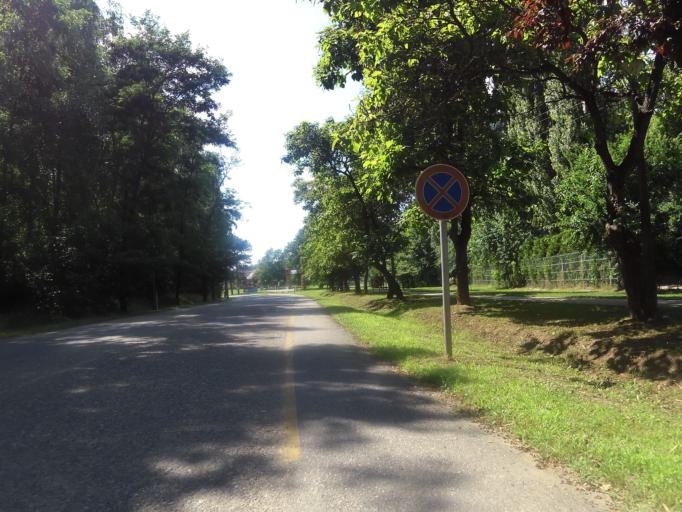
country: HU
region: Jasz-Nagykun-Szolnok
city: Tiszafured
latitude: 47.6219
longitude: 20.7397
